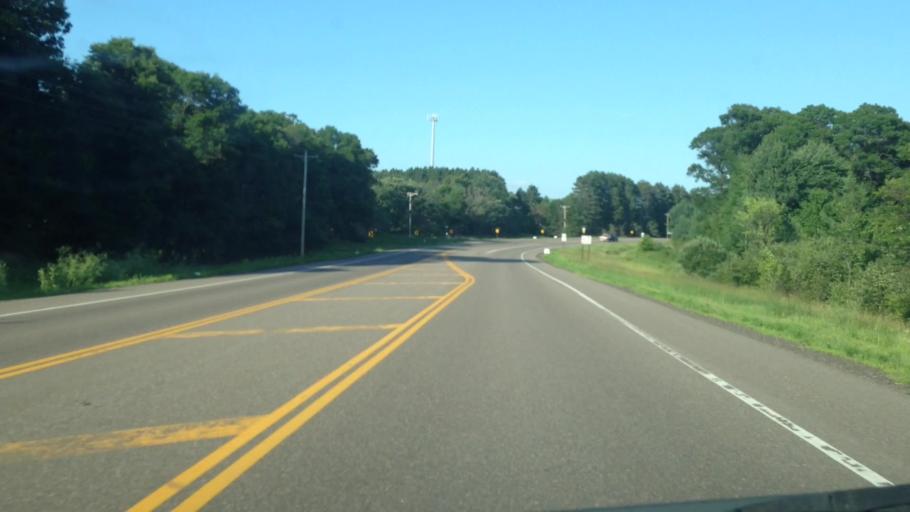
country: US
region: Minnesota
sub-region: Sherburne County
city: Zimmerman
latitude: 45.4446
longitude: -93.6416
